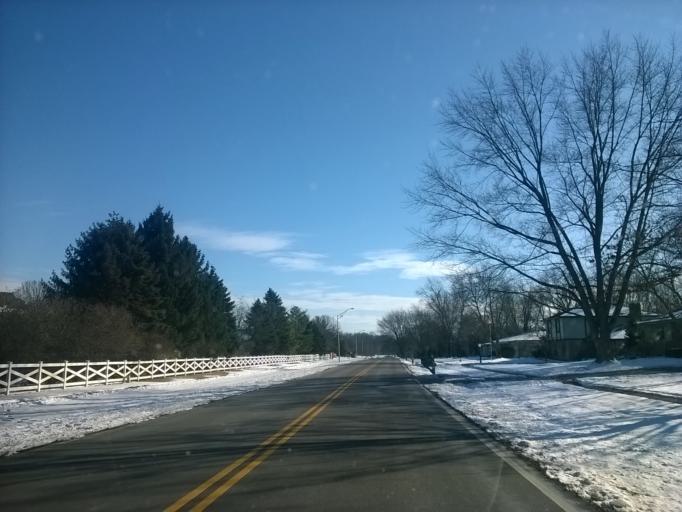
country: US
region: Indiana
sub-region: Hamilton County
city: Carmel
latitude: 39.9477
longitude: -86.0984
